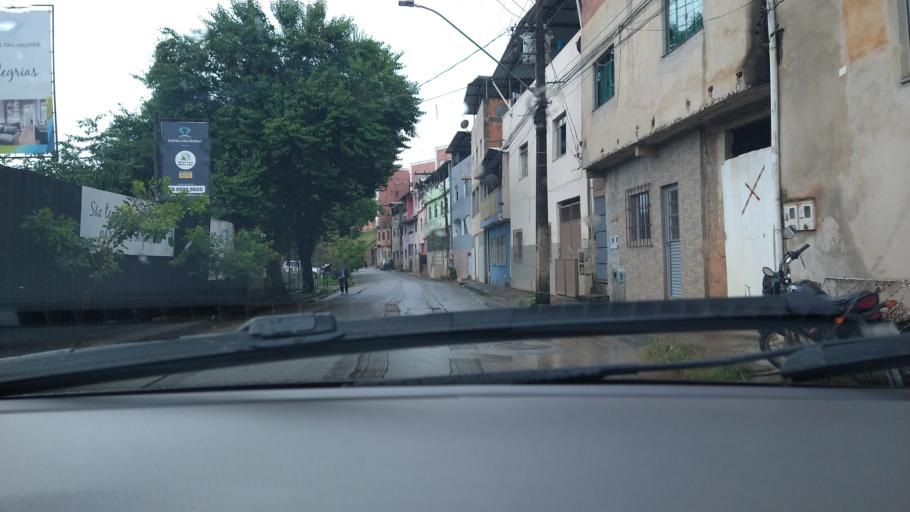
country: BR
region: Minas Gerais
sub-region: Ponte Nova
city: Ponte Nova
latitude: -20.3997
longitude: -42.9008
